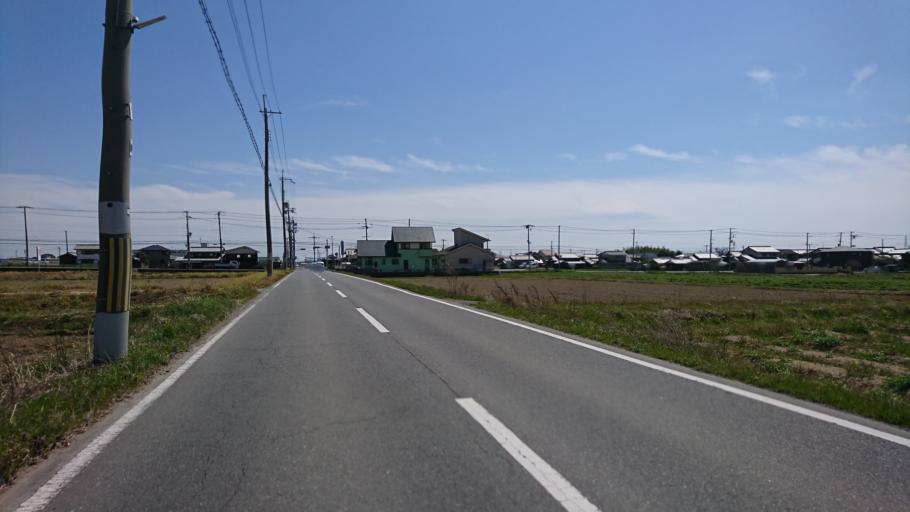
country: JP
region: Hyogo
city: Kakogawacho-honmachi
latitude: 34.7454
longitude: 134.8902
